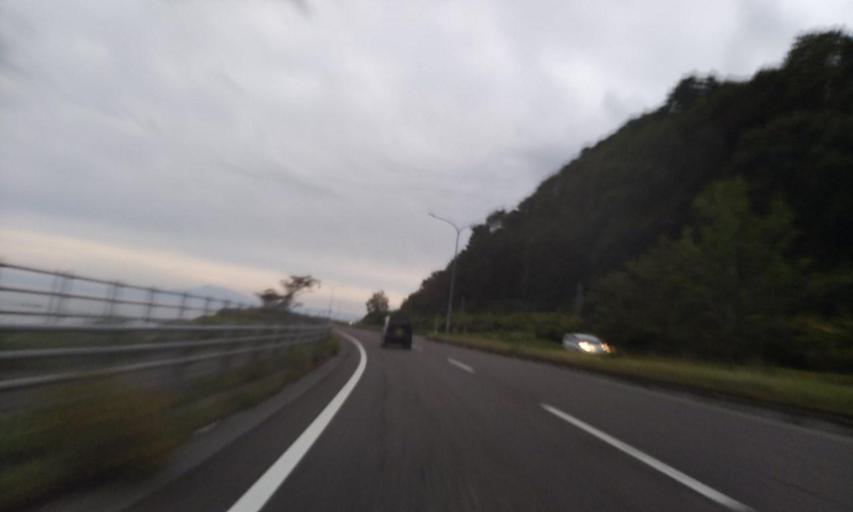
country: JP
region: Hokkaido
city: Abashiri
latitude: 43.9968
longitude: 144.2925
